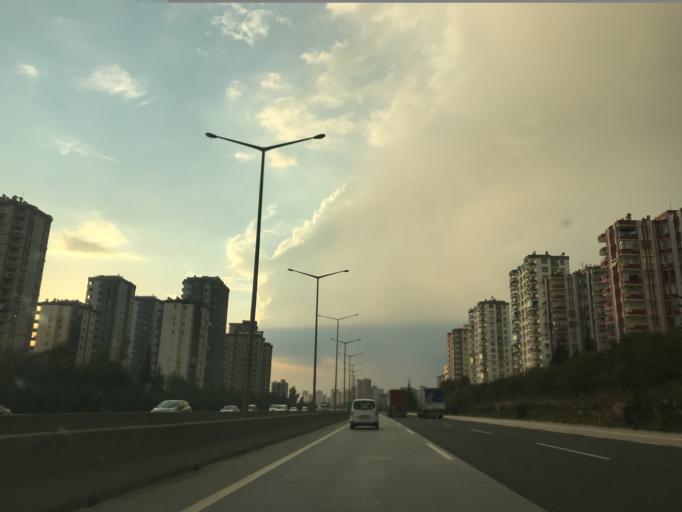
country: TR
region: Adana
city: Seyhan
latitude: 37.0317
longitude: 35.2617
